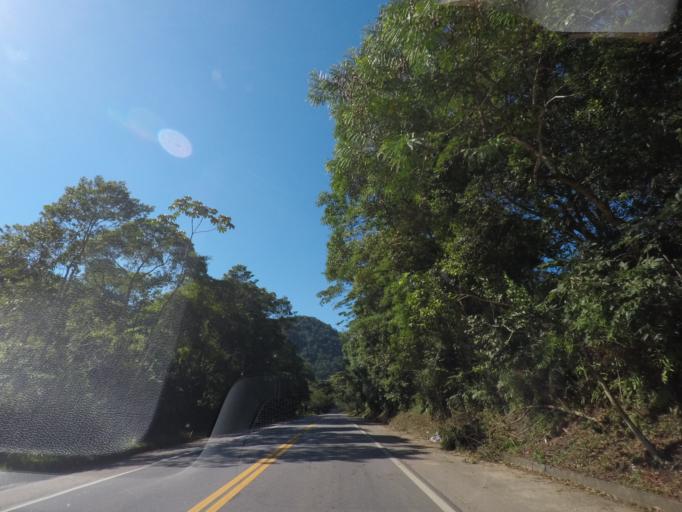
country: BR
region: Rio de Janeiro
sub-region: Parati
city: Paraty
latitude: -23.2995
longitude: -44.7011
